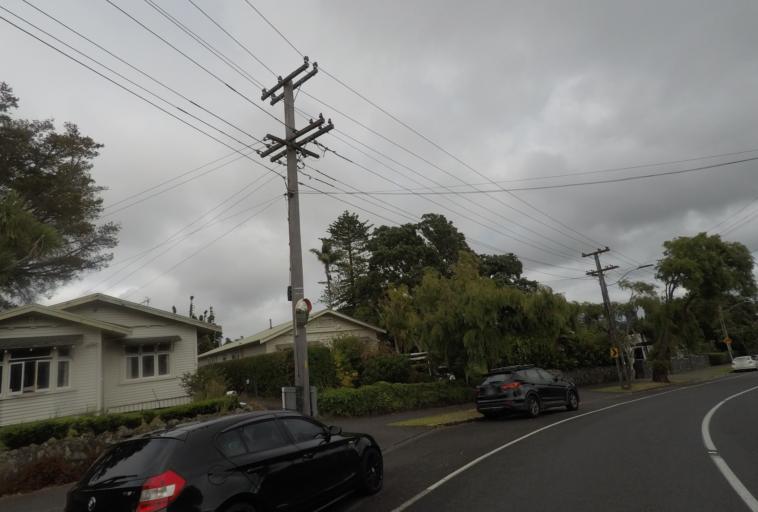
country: NZ
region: Auckland
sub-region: Auckland
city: Auckland
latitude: -36.8793
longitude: 174.7574
